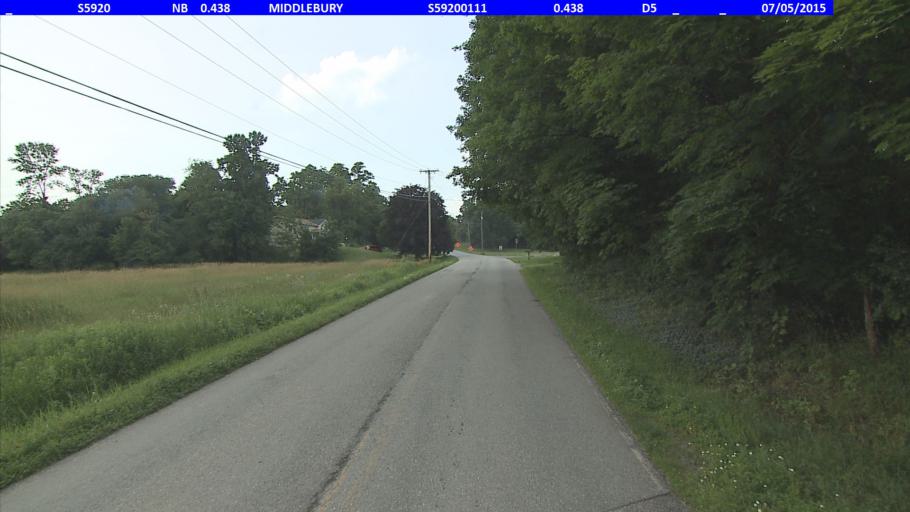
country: US
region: Vermont
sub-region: Addison County
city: Middlebury (village)
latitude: 43.9945
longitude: -73.1344
